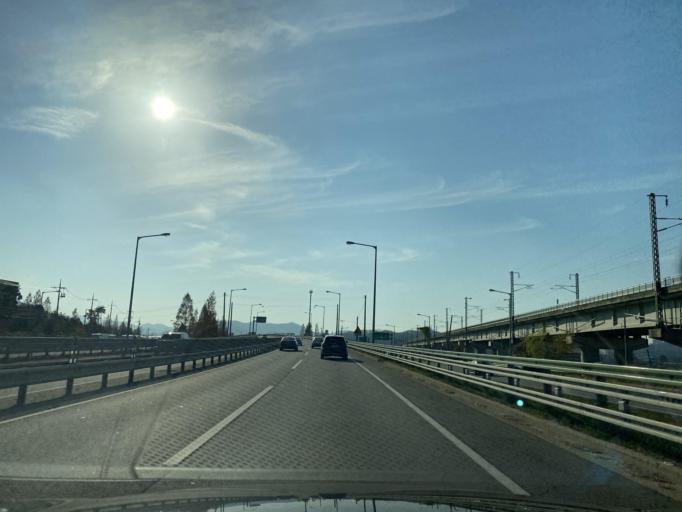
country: KR
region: Chungcheongnam-do
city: Asan
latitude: 36.7744
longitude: 127.0456
